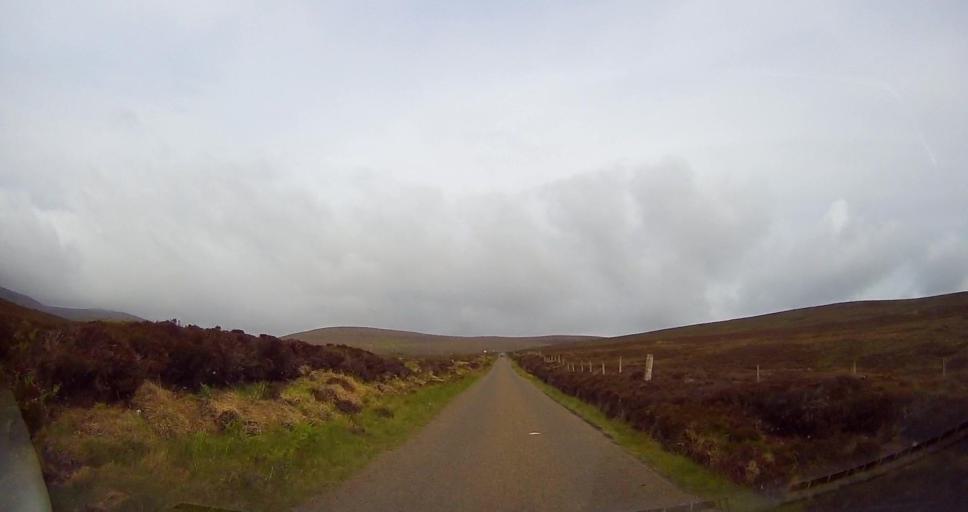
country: GB
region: Scotland
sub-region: Orkney Islands
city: Stromness
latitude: 58.8706
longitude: -3.2322
